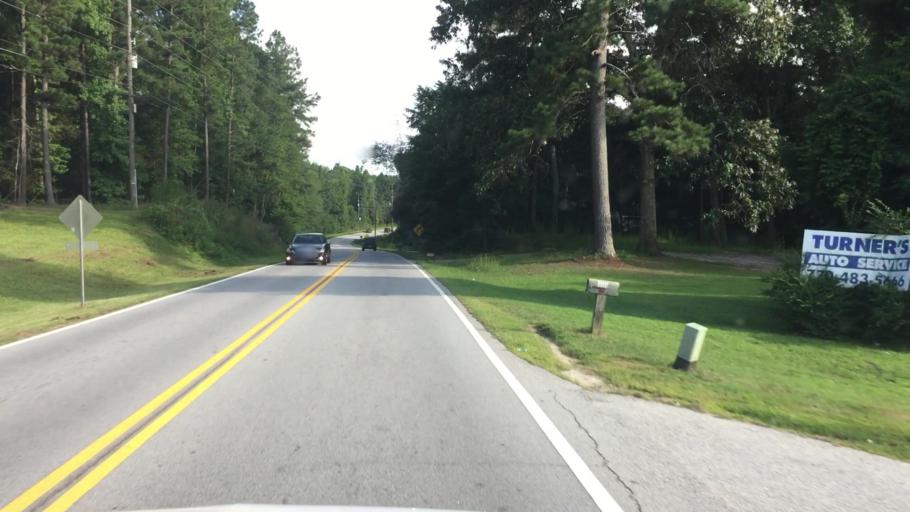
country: US
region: Georgia
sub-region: DeKalb County
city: Pine Mountain
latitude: 33.6063
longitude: -84.1370
